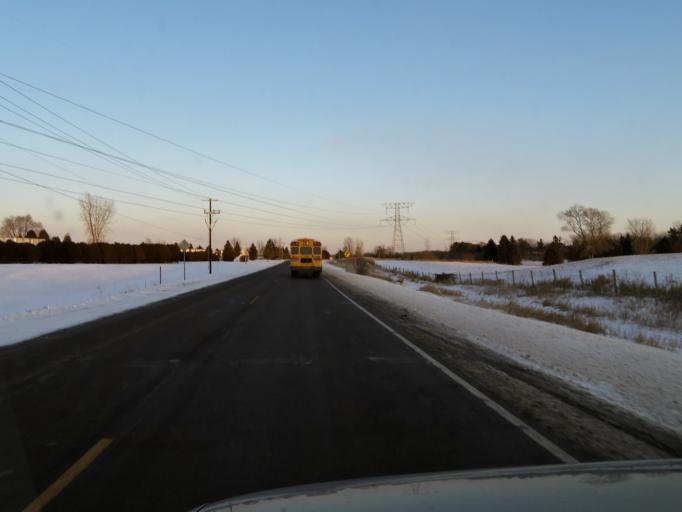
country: US
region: Minnesota
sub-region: Washington County
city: Lake Elmo
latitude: 44.9459
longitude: -92.8525
